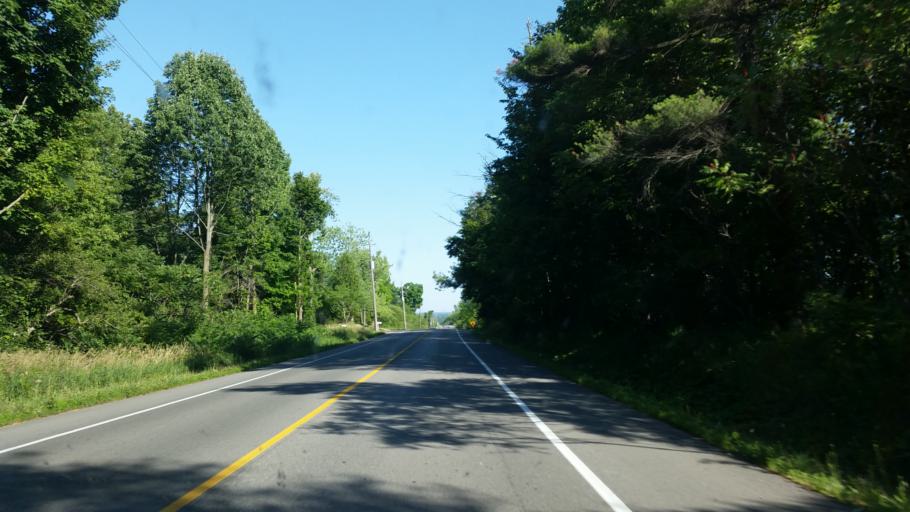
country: CA
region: Ontario
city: Bradford West Gwillimbury
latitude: 43.9606
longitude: -79.7780
